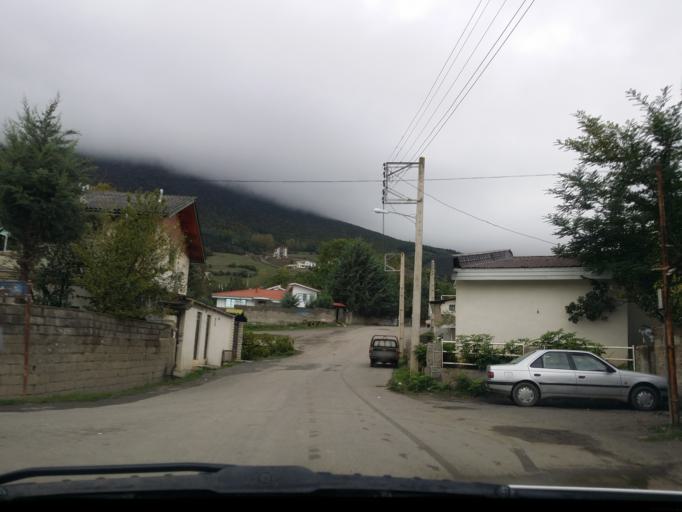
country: IR
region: Mazandaran
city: `Abbasabad
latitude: 36.5065
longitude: 51.1931
